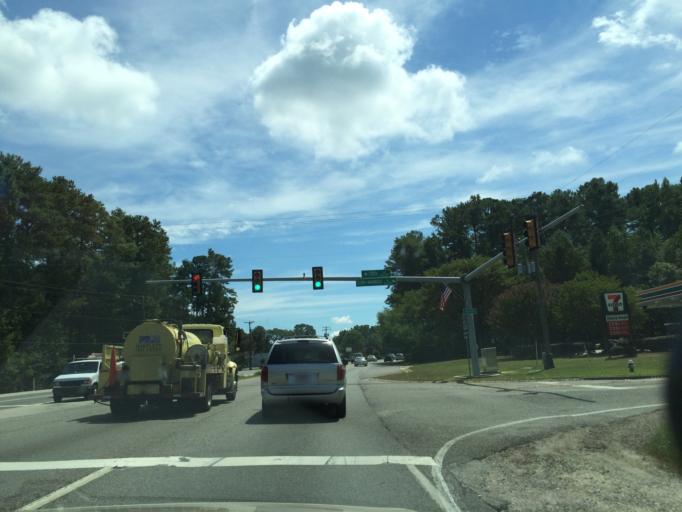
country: US
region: Virginia
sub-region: York County
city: Yorktown
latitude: 37.1978
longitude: -76.4929
